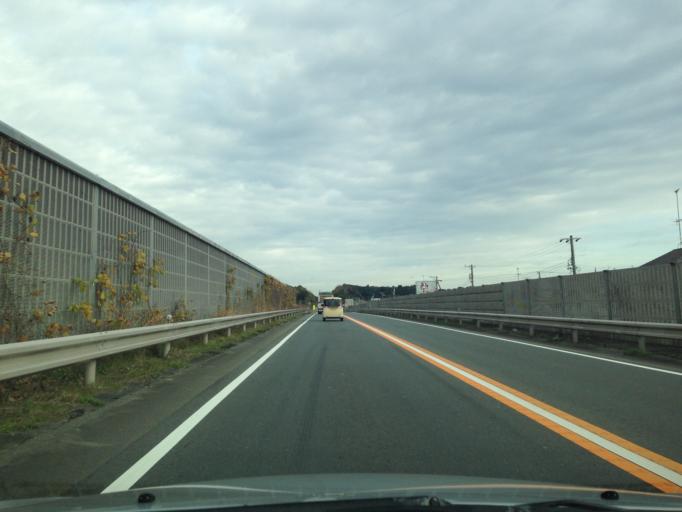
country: JP
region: Shizuoka
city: Kakegawa
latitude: 34.7800
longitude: 137.9946
